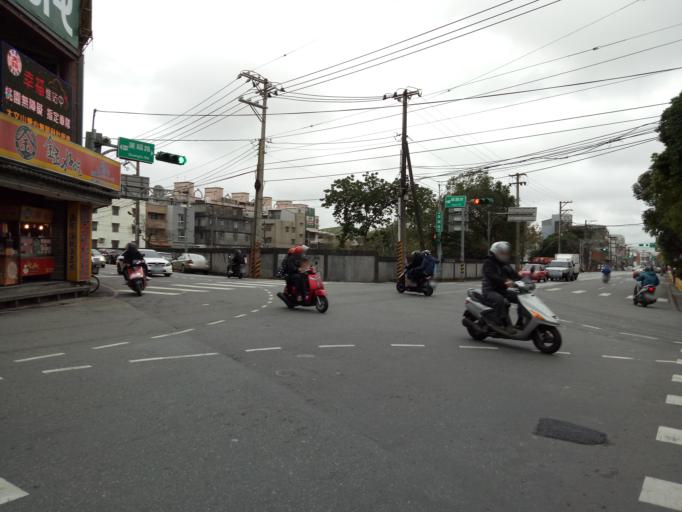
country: TW
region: Taiwan
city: Taoyuan City
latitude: 24.9596
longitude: 121.2944
